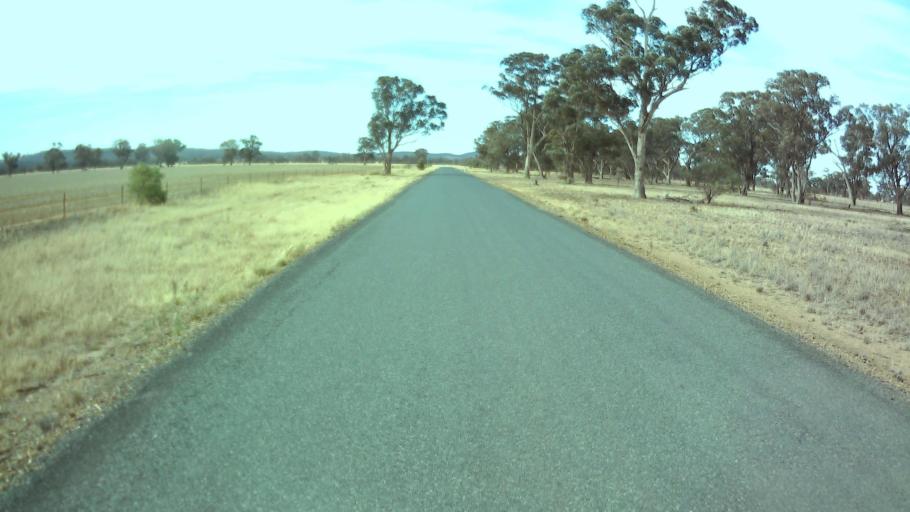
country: AU
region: New South Wales
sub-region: Weddin
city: Grenfell
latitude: -33.8601
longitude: 147.8601
